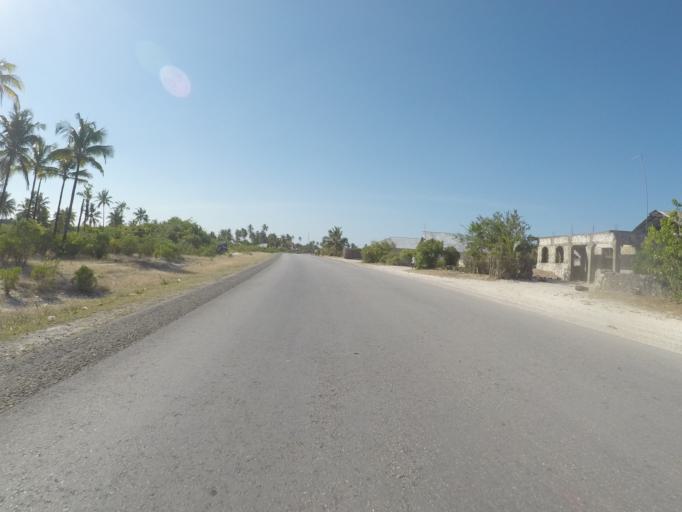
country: TZ
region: Zanzibar Central/South
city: Nganane
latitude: -6.2500
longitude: 39.5327
